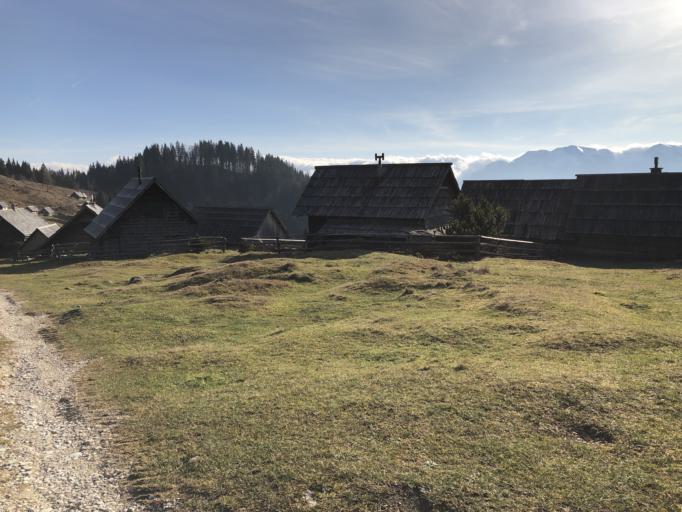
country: SI
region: Bohinj
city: Bohinjska Bistrica
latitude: 46.3136
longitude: 13.9327
